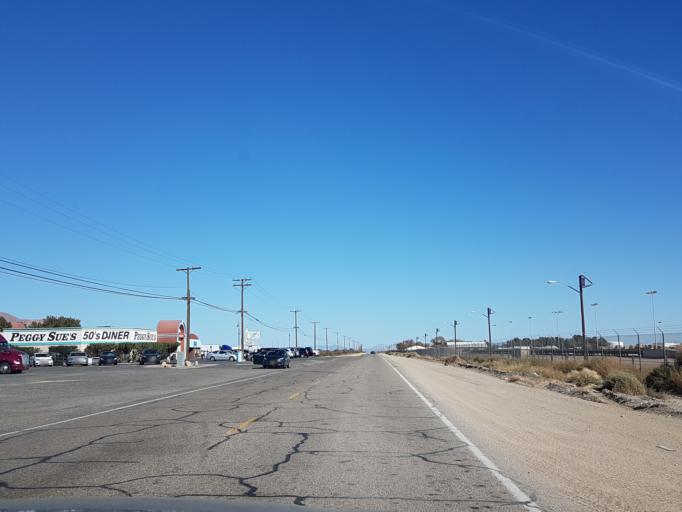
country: US
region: California
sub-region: San Bernardino County
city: Barstow
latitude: 34.9011
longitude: -116.8848
